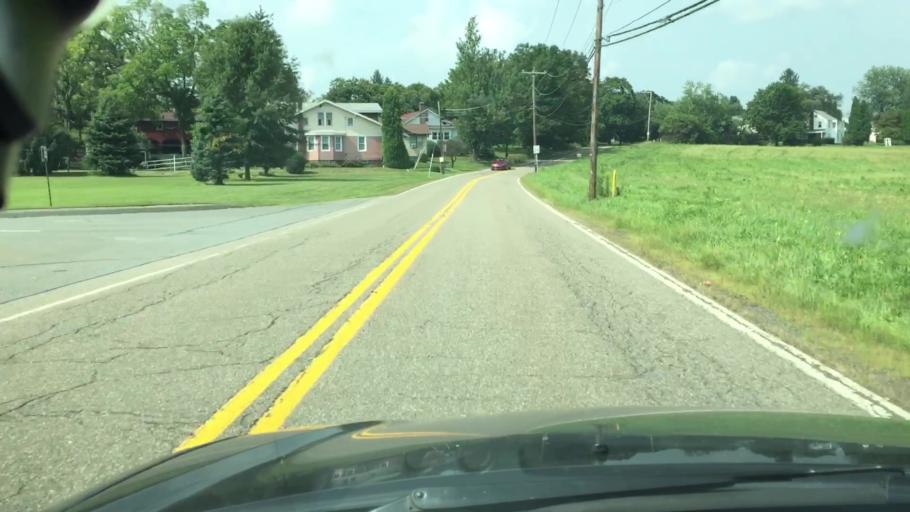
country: US
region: Pennsylvania
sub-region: Luzerne County
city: Harleigh
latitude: 41.0114
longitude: -76.0001
